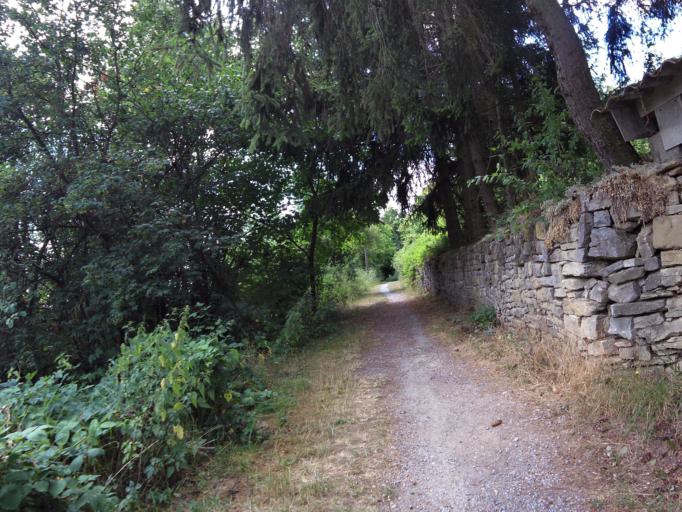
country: DE
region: Bavaria
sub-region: Regierungsbezirk Unterfranken
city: Gerbrunn
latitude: 49.7800
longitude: 9.9912
